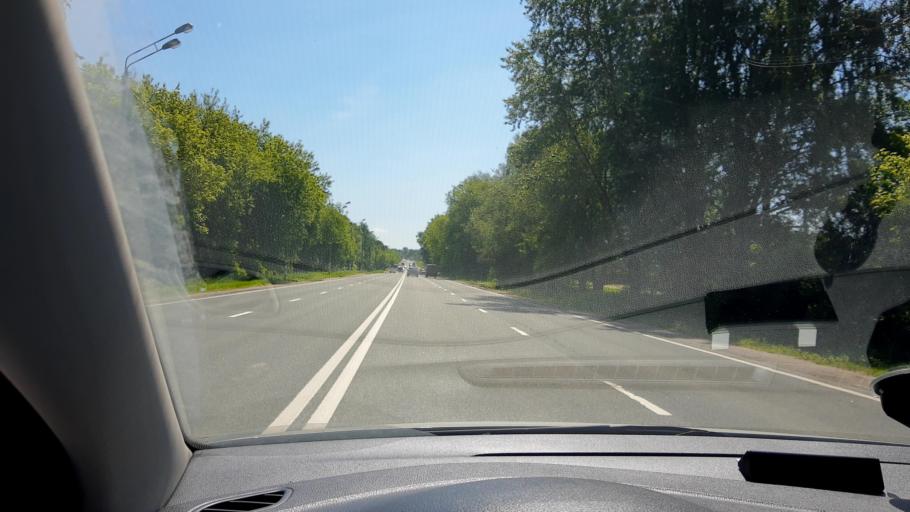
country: RU
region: Moskovskaya
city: Bronnitsy
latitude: 55.4655
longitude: 38.1999
